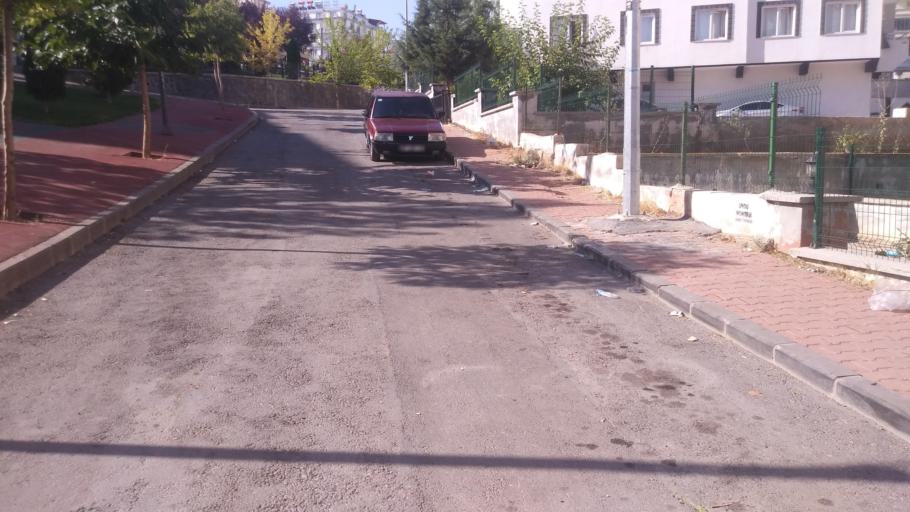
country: TR
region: Gaziantep
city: Sahinbey
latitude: 37.0312
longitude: 37.3357
